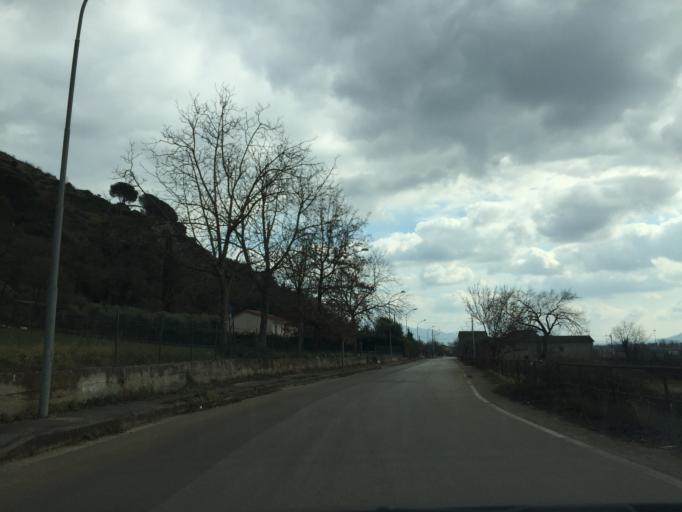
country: IT
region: Latium
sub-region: Provincia di Frosinone
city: Villa Santa Lucia
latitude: 41.4929
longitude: 13.7811
